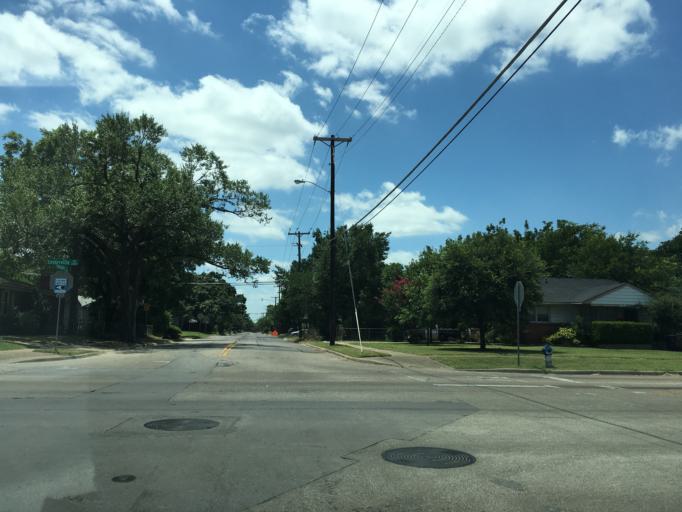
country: US
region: Texas
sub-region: Dallas County
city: Garland
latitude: 32.8430
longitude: -96.6731
